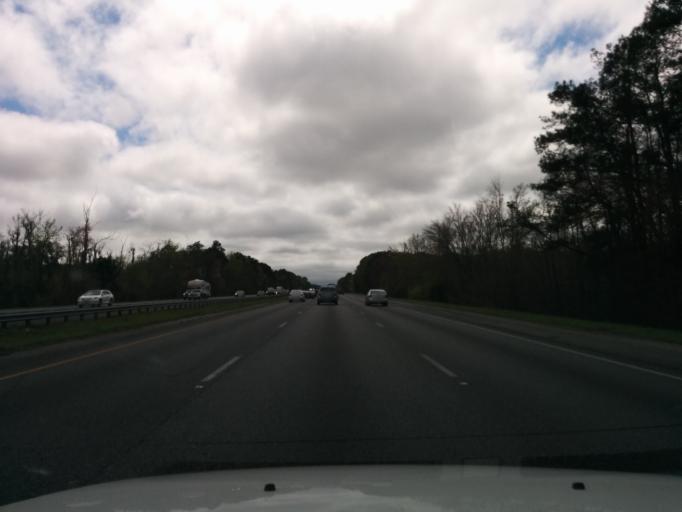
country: US
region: Georgia
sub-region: Chatham County
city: Pooler
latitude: 32.0542
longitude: -81.2562
